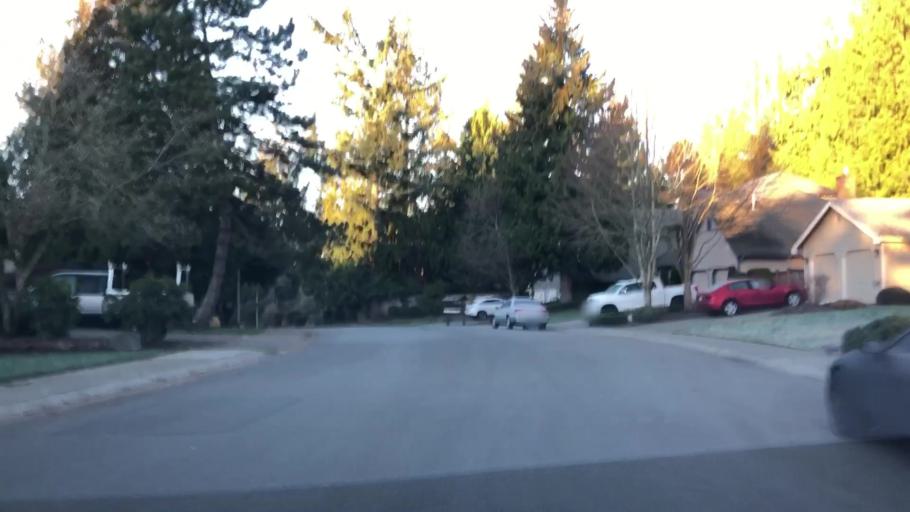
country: US
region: Washington
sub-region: King County
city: Cottage Lake
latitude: 47.7238
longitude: -122.1068
